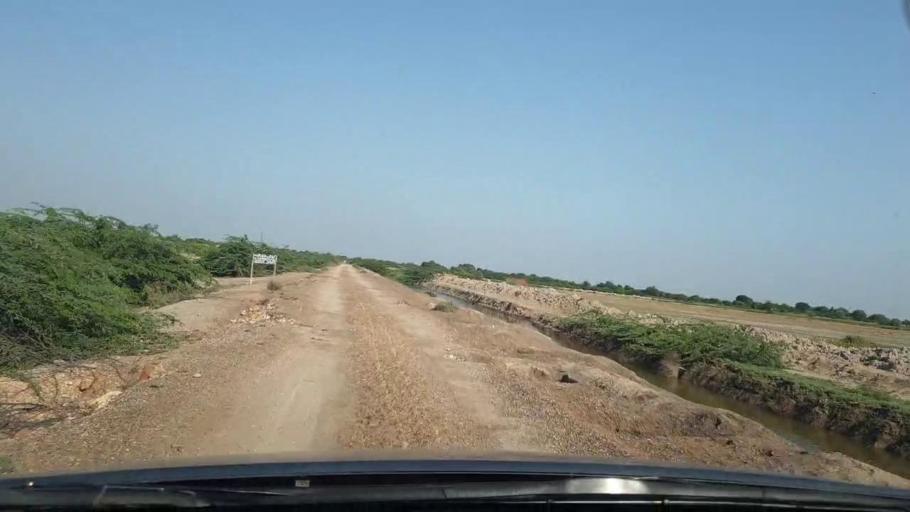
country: PK
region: Sindh
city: Naukot
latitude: 24.8335
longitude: 69.2576
